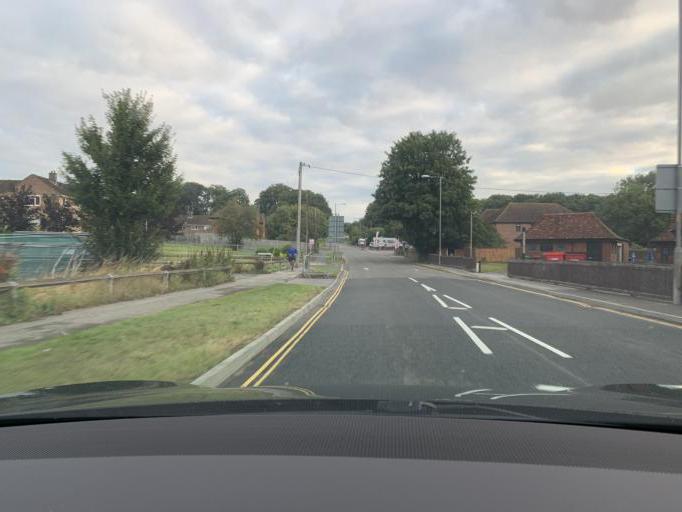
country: GB
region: England
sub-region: Wiltshire
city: Tidworth
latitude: 51.2417
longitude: -1.6646
